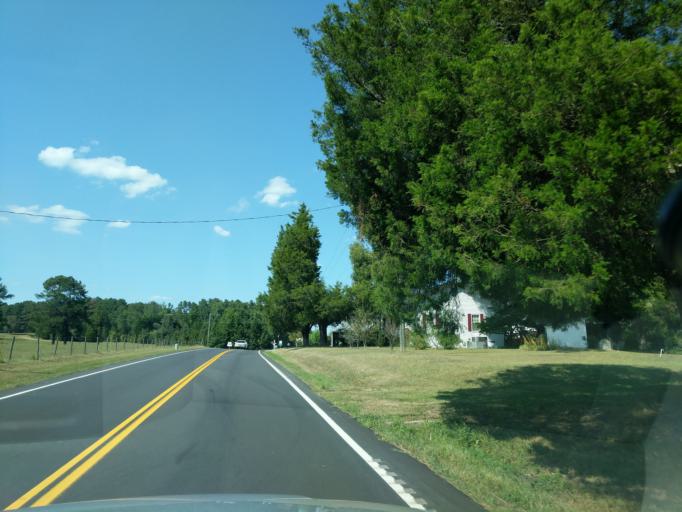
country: US
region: South Carolina
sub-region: Lexington County
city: Leesville
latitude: 33.9600
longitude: -81.5306
